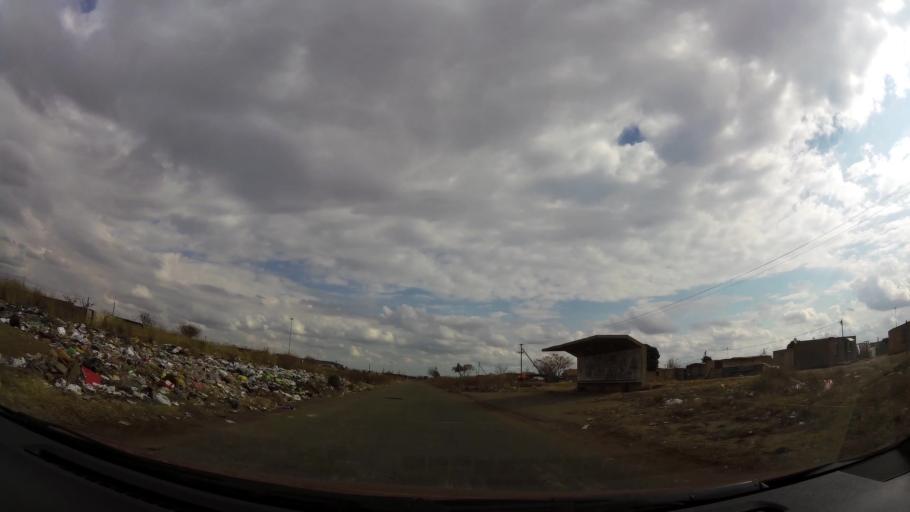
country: ZA
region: Gauteng
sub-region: Sedibeng District Municipality
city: Vanderbijlpark
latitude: -26.6799
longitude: 27.7889
